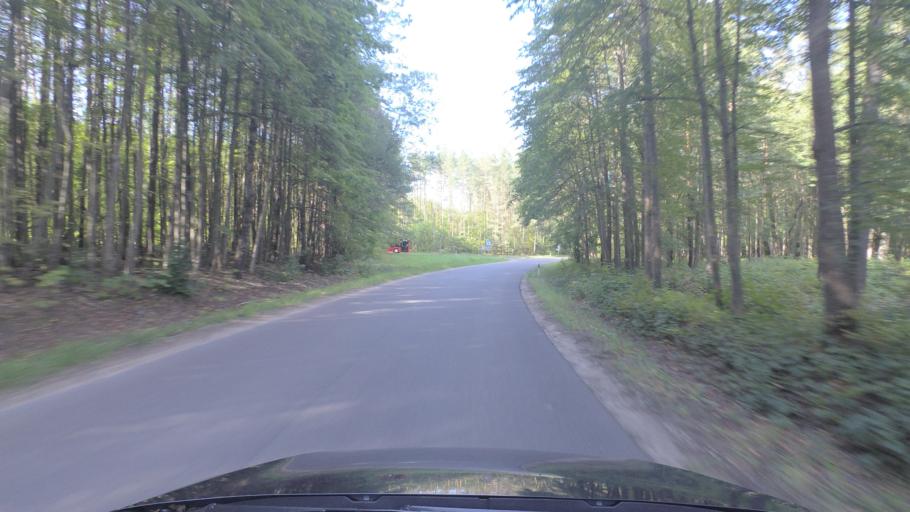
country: LT
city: Nemencine
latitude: 54.8233
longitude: 25.3569
